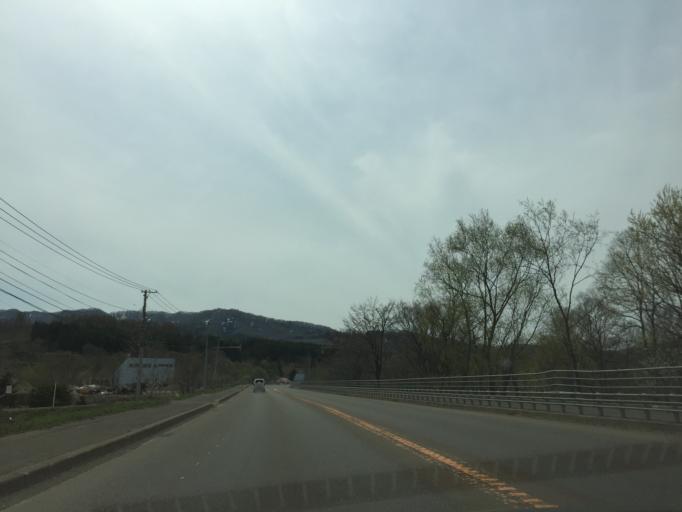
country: JP
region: Hokkaido
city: Akabira
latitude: 43.5397
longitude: 142.1052
